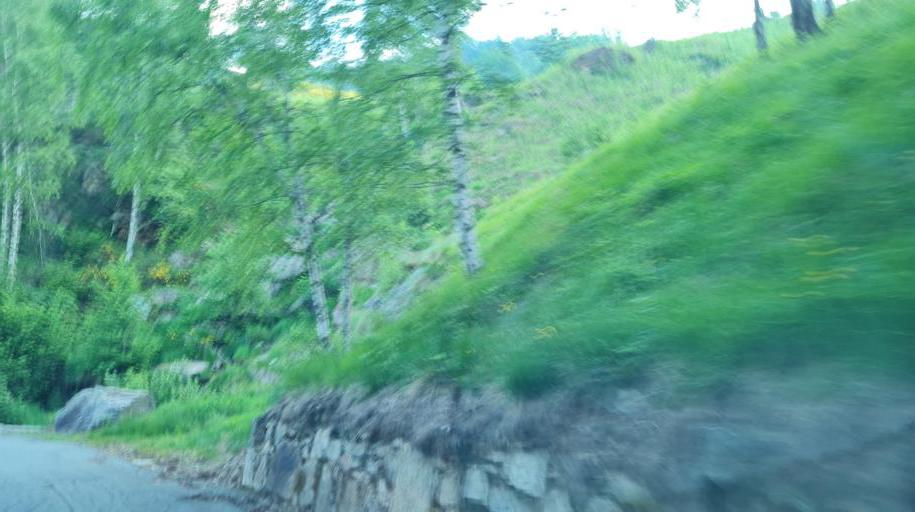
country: IT
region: Piedmont
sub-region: Provincia di Biella
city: Sordevolo
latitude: 45.5928
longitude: 7.9557
